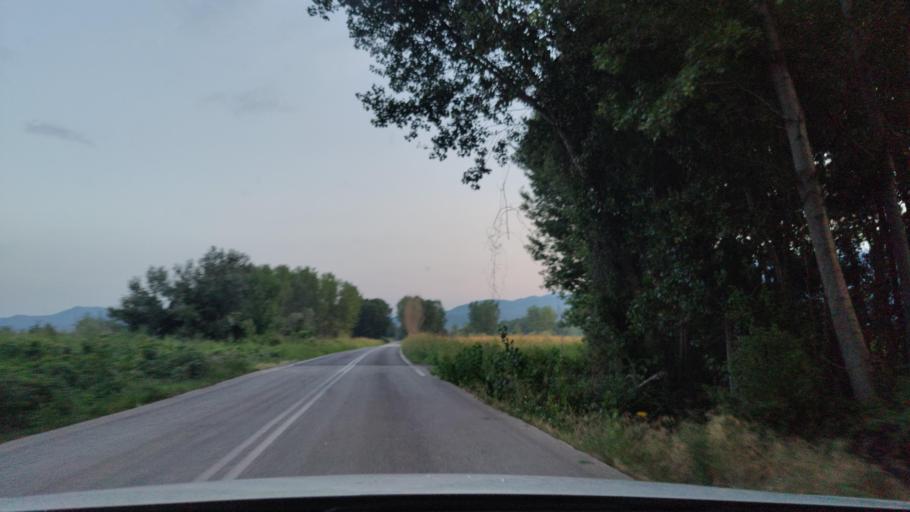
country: GR
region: Central Macedonia
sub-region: Nomos Serron
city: Chrysochorafa
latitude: 41.1616
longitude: 23.2451
